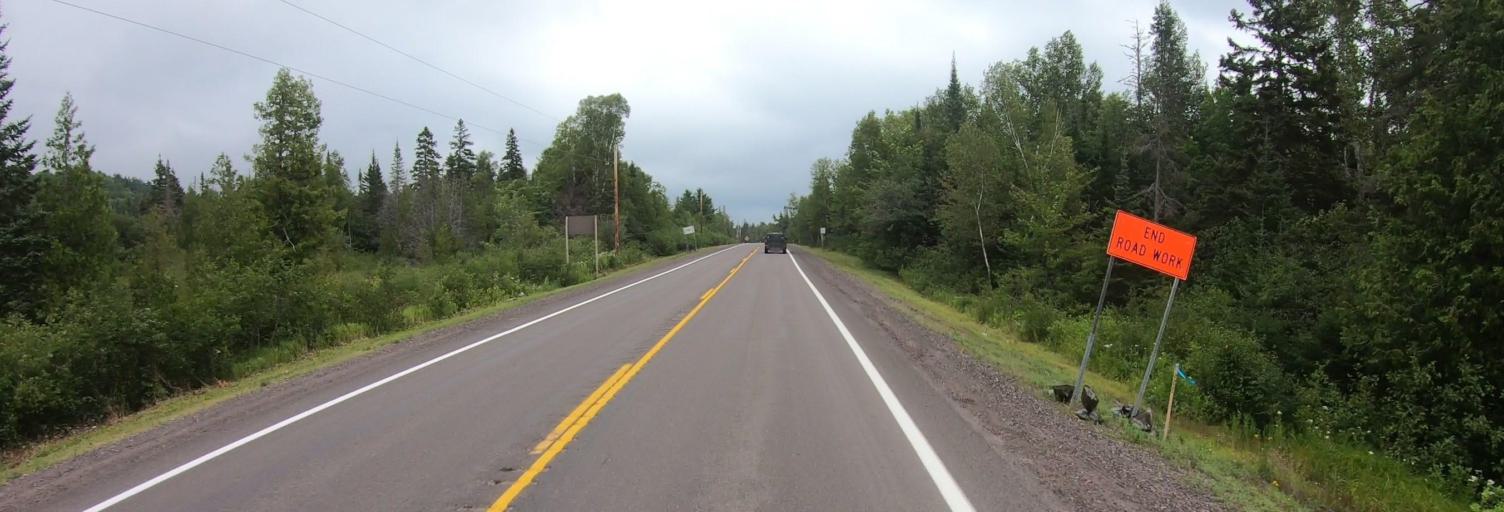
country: US
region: Michigan
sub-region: Keweenaw County
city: Eagle River
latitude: 47.4047
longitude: -88.1952
